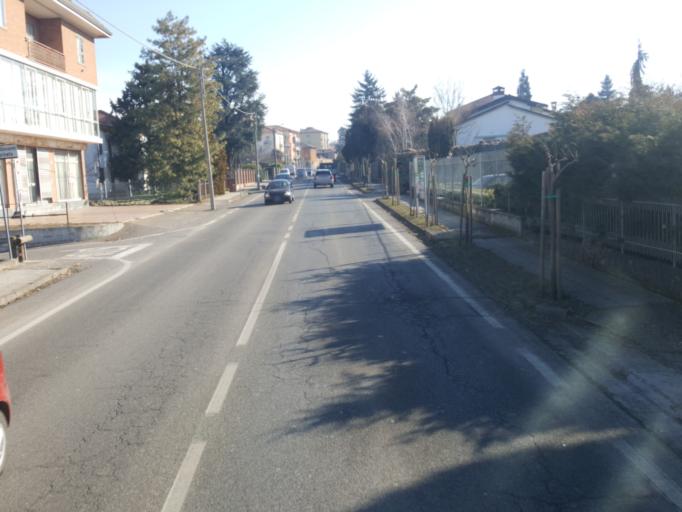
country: IT
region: Piedmont
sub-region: Provincia di Alessandria
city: Viguzzolo
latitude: 44.9074
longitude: 8.9136
